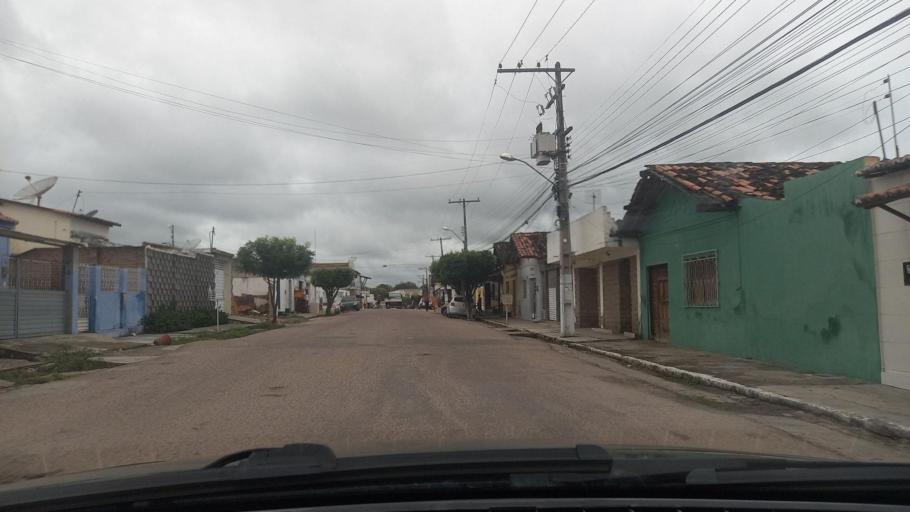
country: BR
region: Alagoas
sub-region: Delmiro Gouveia
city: Delmiro Gouveia
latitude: -9.3867
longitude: -37.9953
